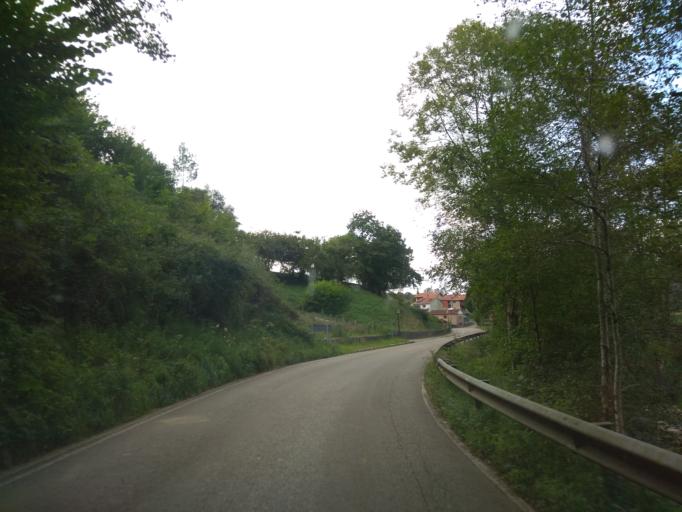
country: ES
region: Cantabria
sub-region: Provincia de Cantabria
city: Comillas
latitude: 43.3193
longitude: -4.3424
